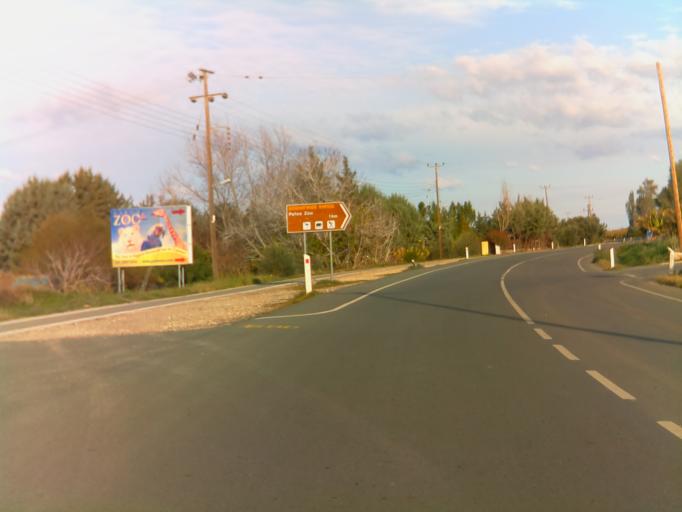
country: CY
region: Pafos
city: Pegeia
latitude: 34.8909
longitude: 32.3365
